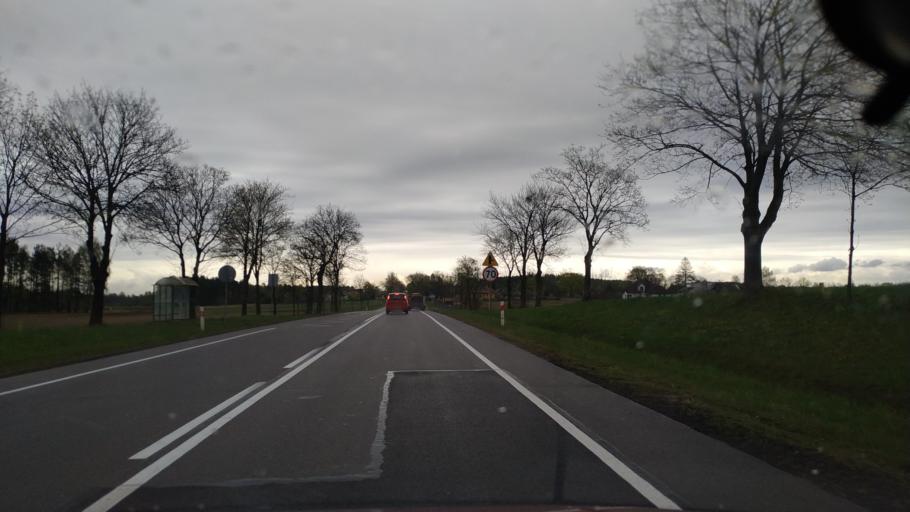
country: PL
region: Pomeranian Voivodeship
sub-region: Powiat chojnicki
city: Czersk
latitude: 53.8103
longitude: 18.0251
